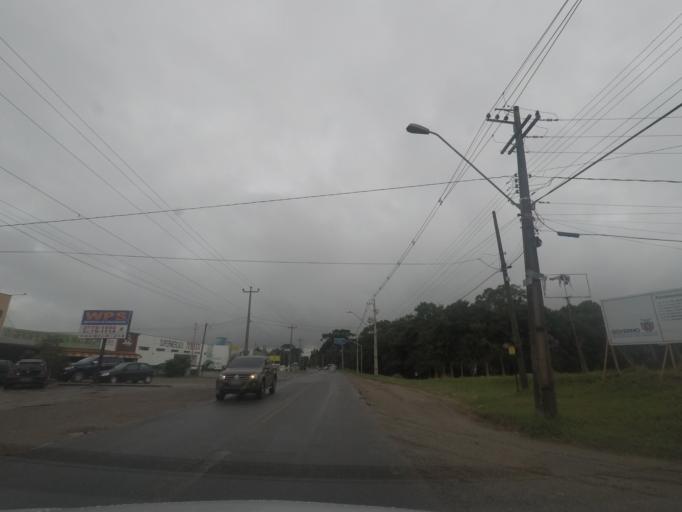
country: BR
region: Parana
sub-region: Quatro Barras
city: Quatro Barras
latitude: -25.3448
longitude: -49.0842
